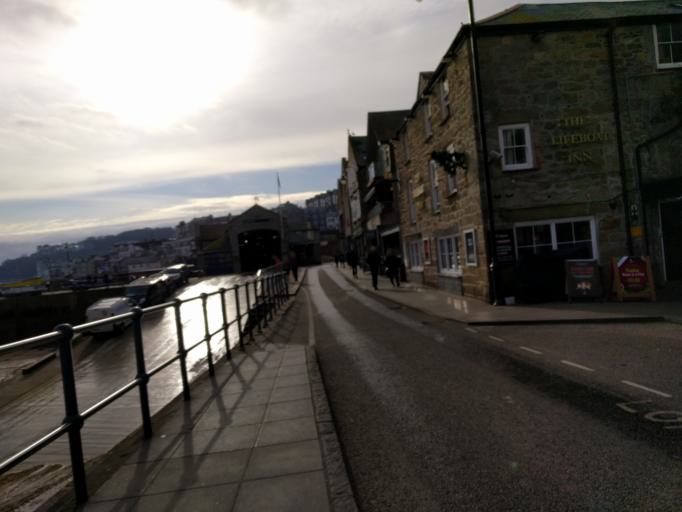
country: GB
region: England
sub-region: Cornwall
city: St Ives
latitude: 50.2134
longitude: -5.4799
